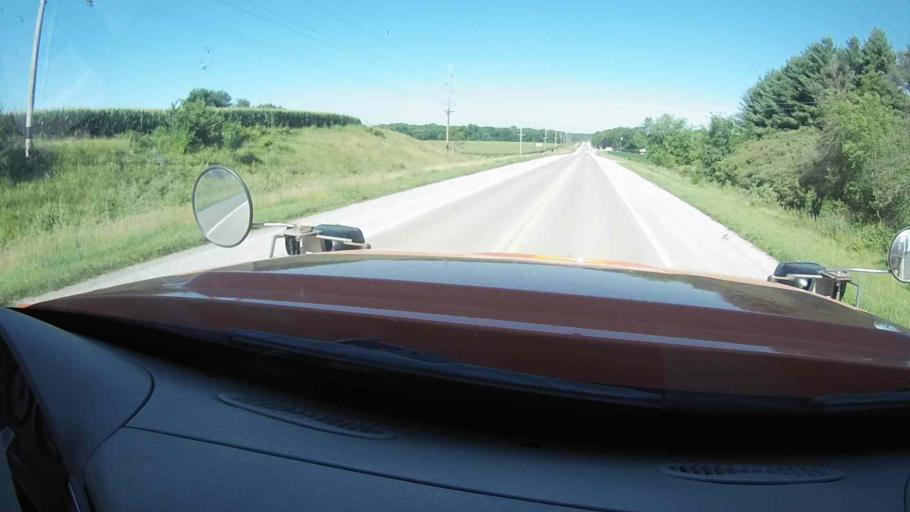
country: US
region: Iowa
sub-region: Johnson County
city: Lone Tree
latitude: 41.4964
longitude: -91.4971
